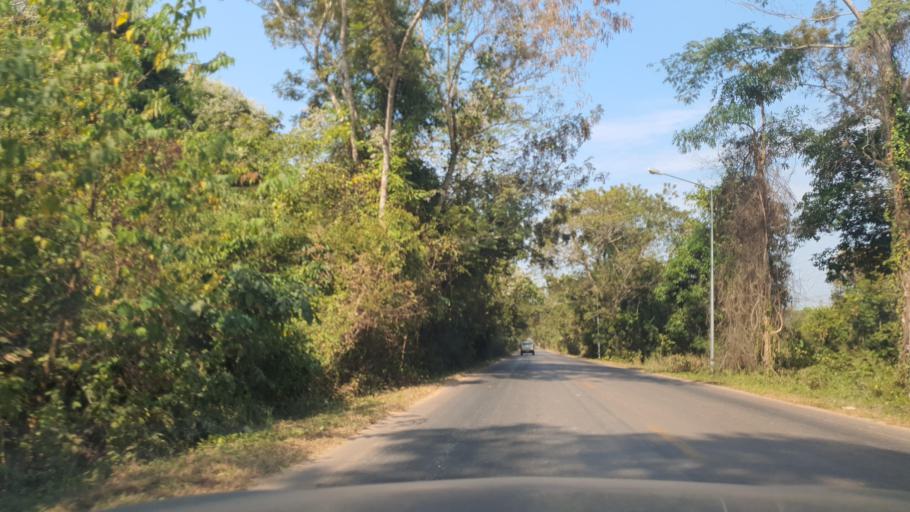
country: TH
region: Nakhon Phanom
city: Ban Phaeng
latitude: 18.0178
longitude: 104.1532
